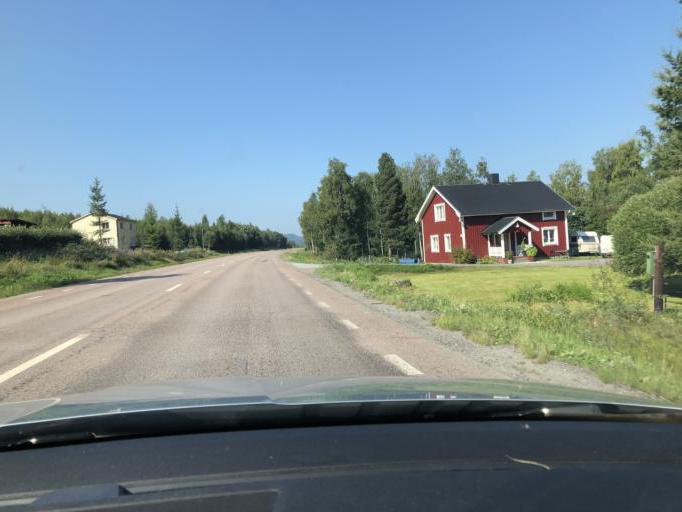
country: SE
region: Vaesternorrland
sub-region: OErnskoeldsviks Kommun
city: Bjasta
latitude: 63.2937
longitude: 18.5529
